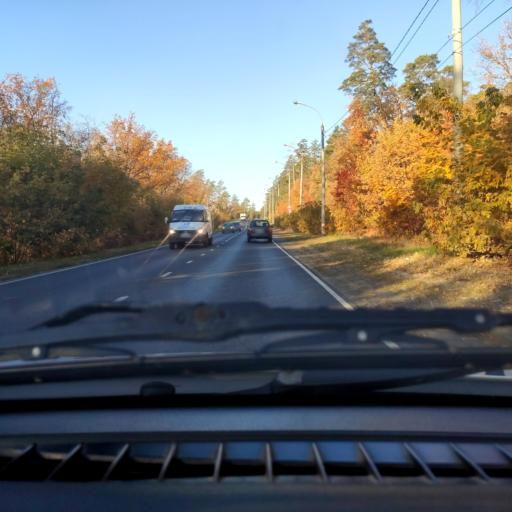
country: RU
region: Samara
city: Tol'yatti
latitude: 53.4733
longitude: 49.3913
